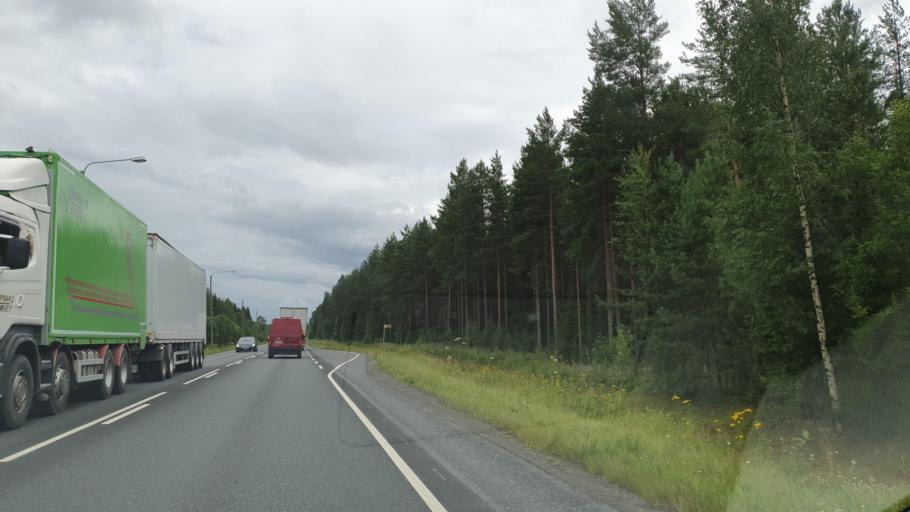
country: FI
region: Northern Savo
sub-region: Ylae-Savo
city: Lapinlahti
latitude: 63.4450
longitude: 27.3220
